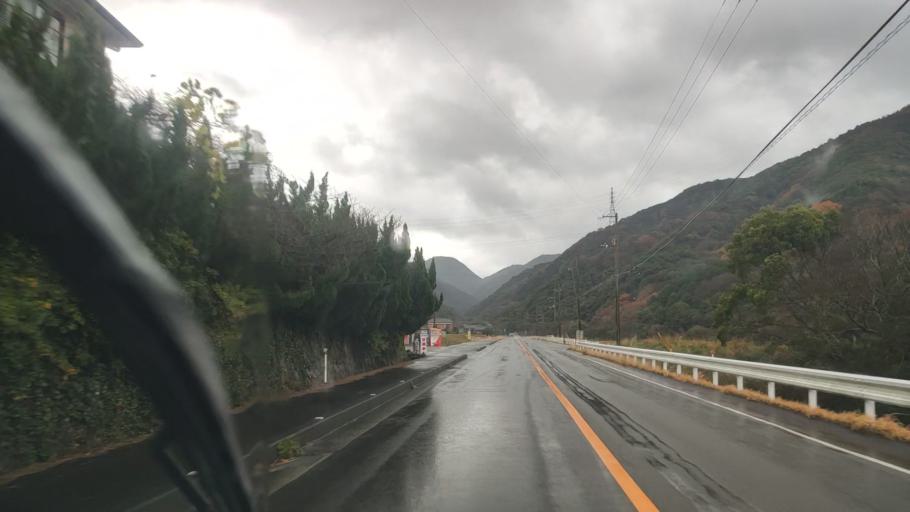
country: JP
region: Tokushima
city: Kamojimacho-jogejima
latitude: 34.1956
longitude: 134.3328
